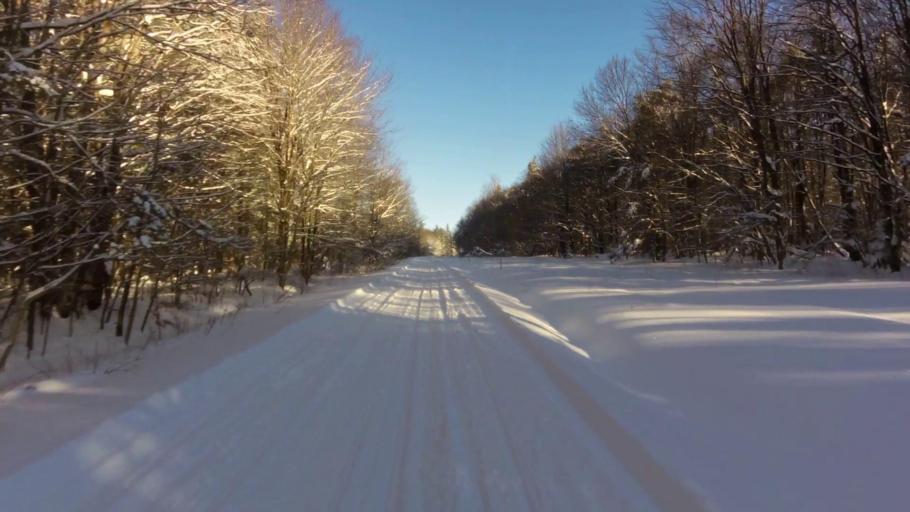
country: US
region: New York
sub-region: Chautauqua County
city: Falconer
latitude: 42.2368
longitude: -79.2178
